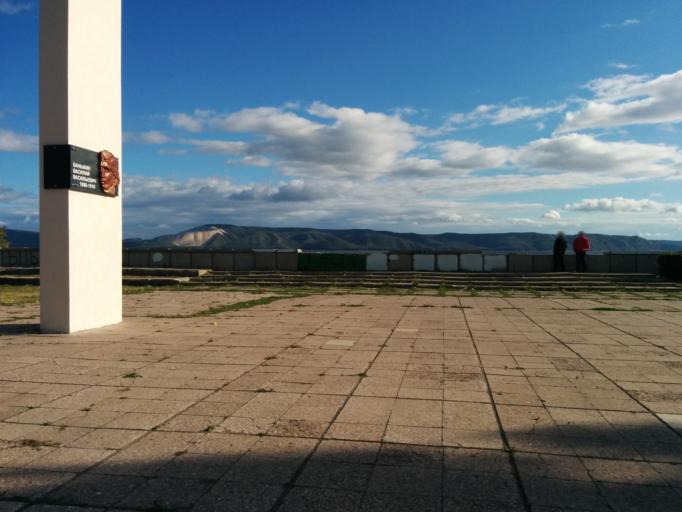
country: RU
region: Samara
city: Tol'yatti
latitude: 53.4740
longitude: 49.3492
